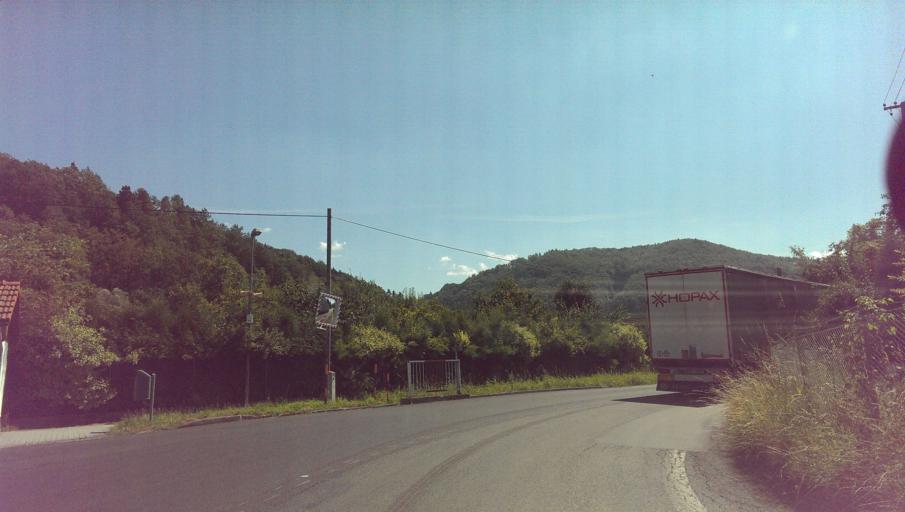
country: CZ
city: Lichnov (o. Novy Jicin)
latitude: 49.5918
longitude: 18.1913
